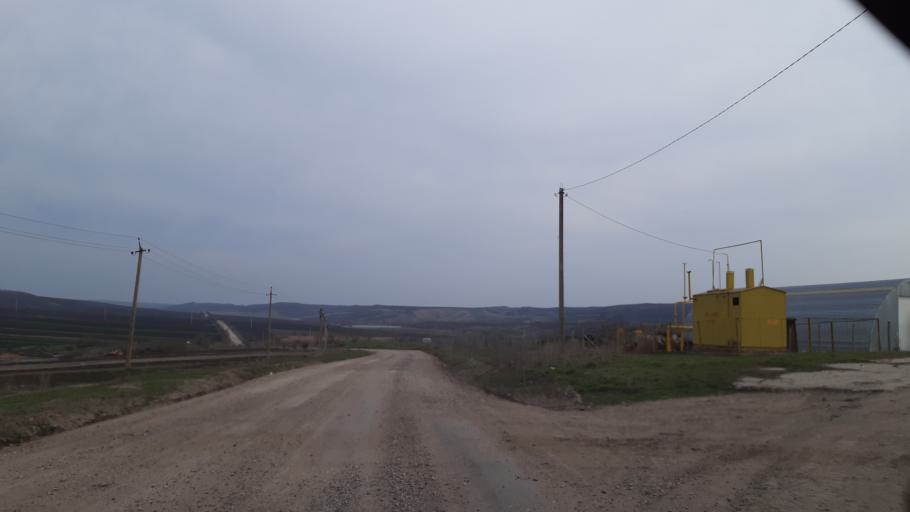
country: MD
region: Soldanesti
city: Soldanesti
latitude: 47.7084
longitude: 28.7096
